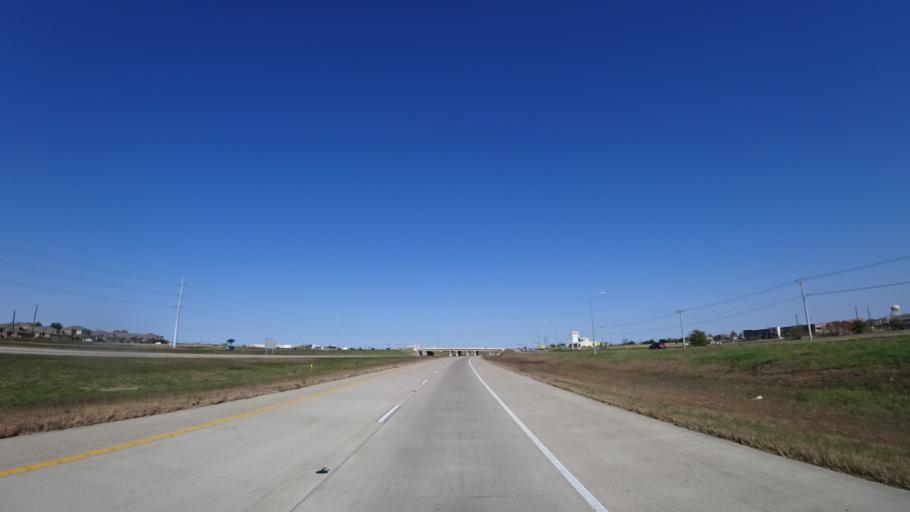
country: US
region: Texas
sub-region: Williamson County
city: Hutto
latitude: 30.4967
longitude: -97.5824
